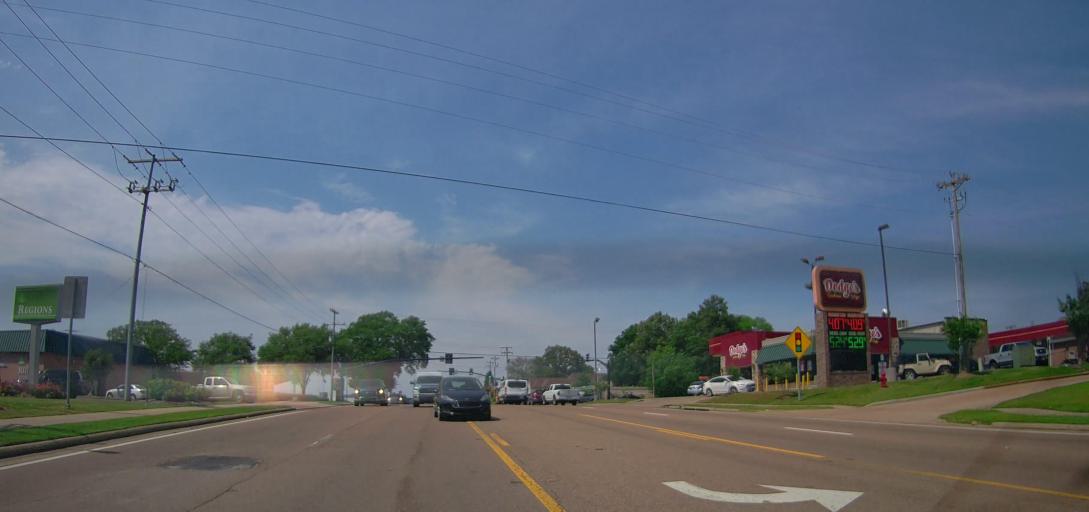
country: US
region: Mississippi
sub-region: De Soto County
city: Olive Branch
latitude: 34.9610
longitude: -89.8304
